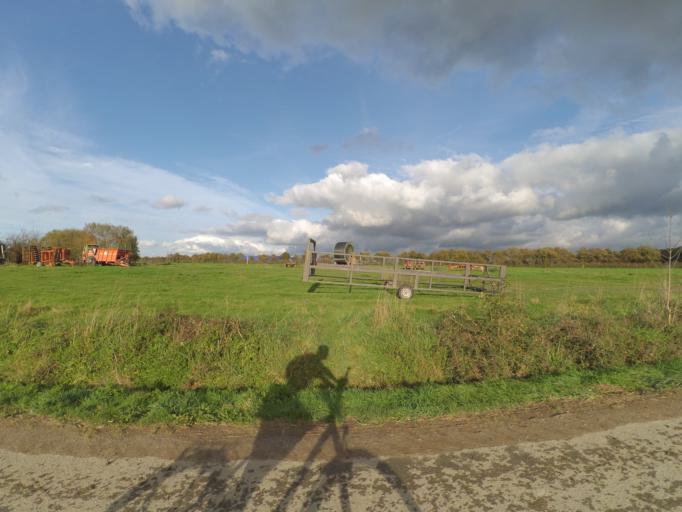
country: FR
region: Pays de la Loire
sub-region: Departement de la Vendee
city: Saint-Hilaire-de-Loulay
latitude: 47.0165
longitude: -1.3566
